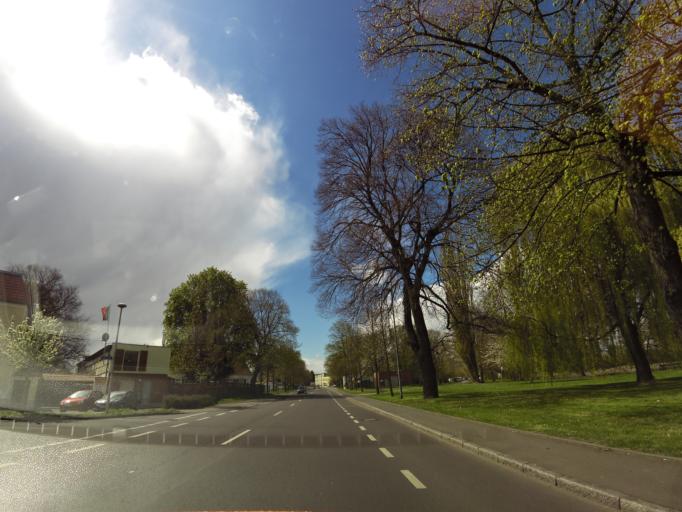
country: DE
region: Saxony-Anhalt
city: Diesdorf
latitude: 52.0996
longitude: 11.5779
